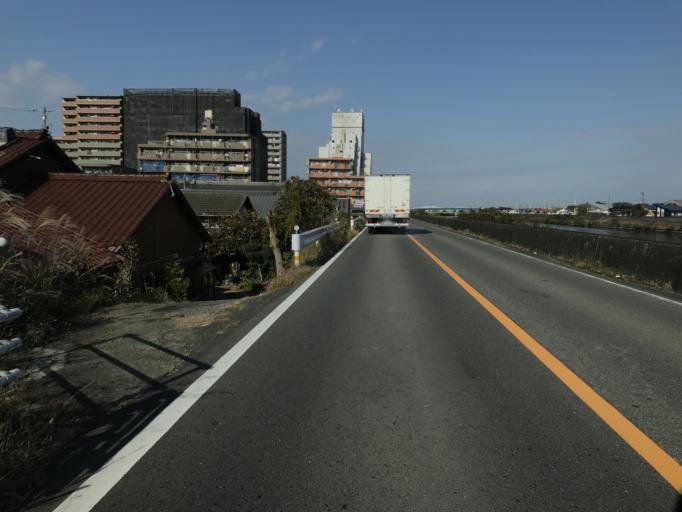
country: JP
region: Aichi
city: Kanie
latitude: 35.1616
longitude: 136.8256
